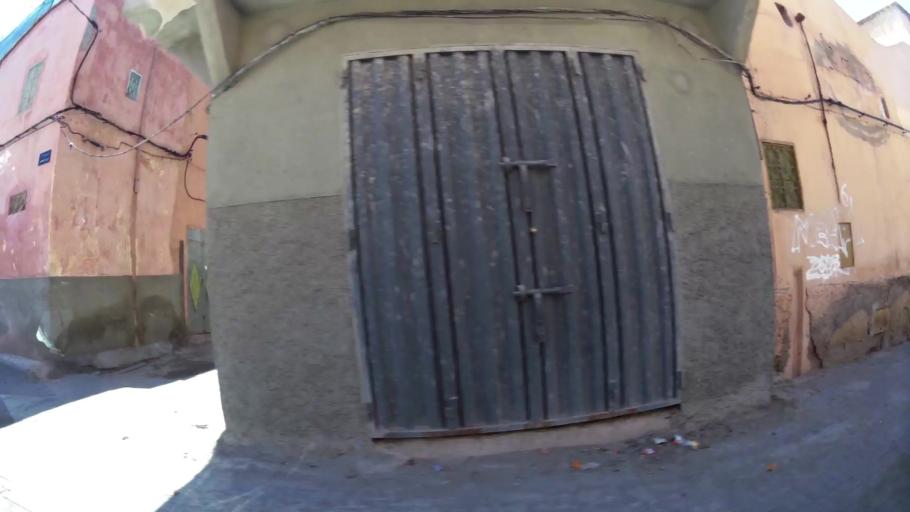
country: MA
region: Marrakech-Tensift-Al Haouz
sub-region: Marrakech
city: Marrakesh
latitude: 31.6364
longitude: -8.0443
